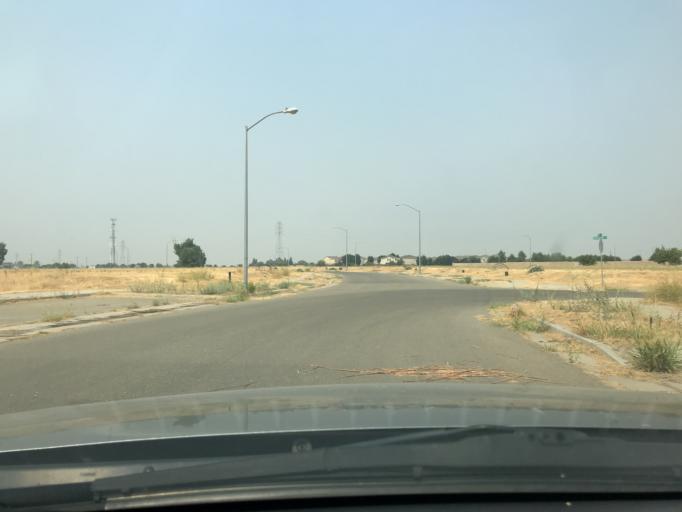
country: US
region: California
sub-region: Merced County
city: Merced
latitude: 37.3451
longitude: -120.4700
